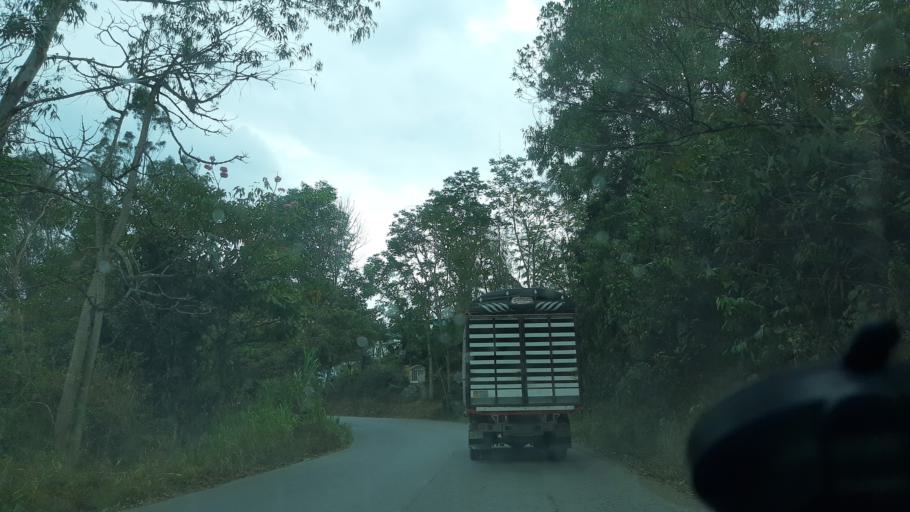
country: CO
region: Boyaca
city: Garagoa
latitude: 5.0780
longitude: -73.3707
